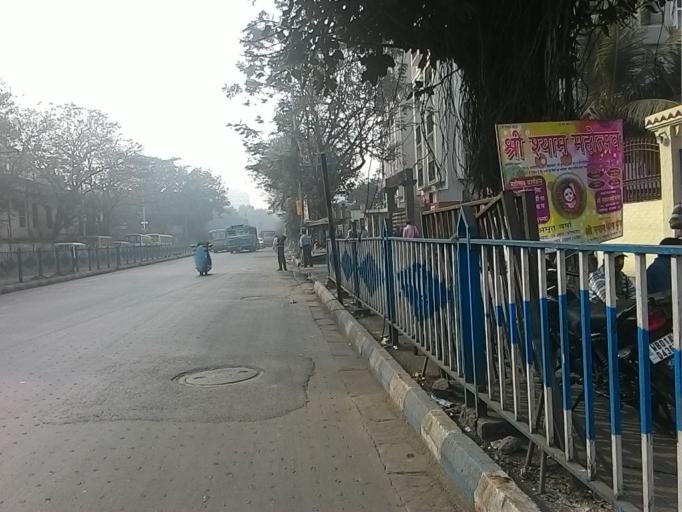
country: IN
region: West Bengal
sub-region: Kolkata
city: Bara Bazar
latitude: 22.5360
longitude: 88.3275
